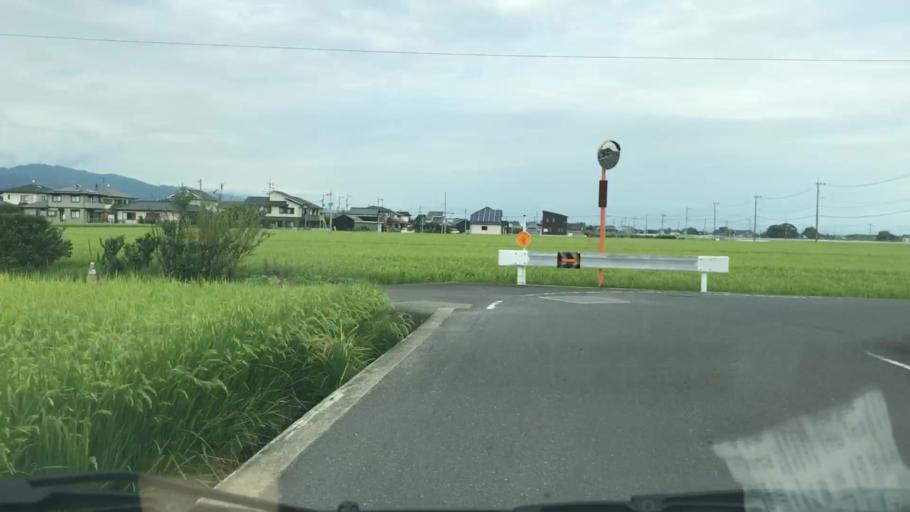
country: JP
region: Saga Prefecture
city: Saga-shi
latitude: 33.2907
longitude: 130.2300
